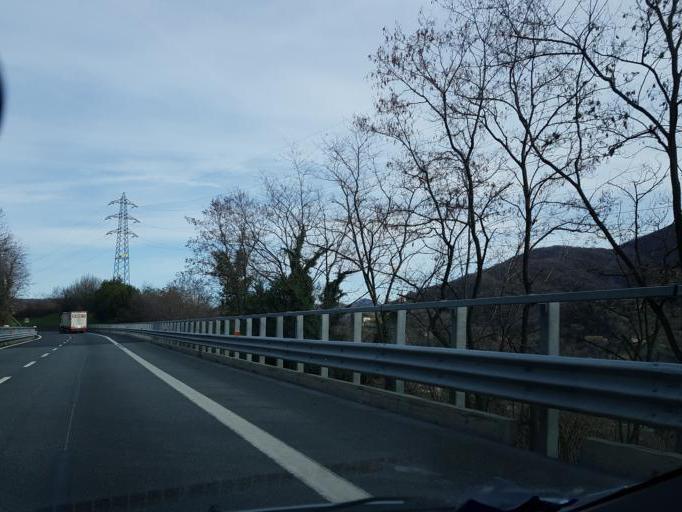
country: IT
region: Liguria
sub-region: Provincia di Genova
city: Pedemonte
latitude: 44.4913
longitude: 8.9175
